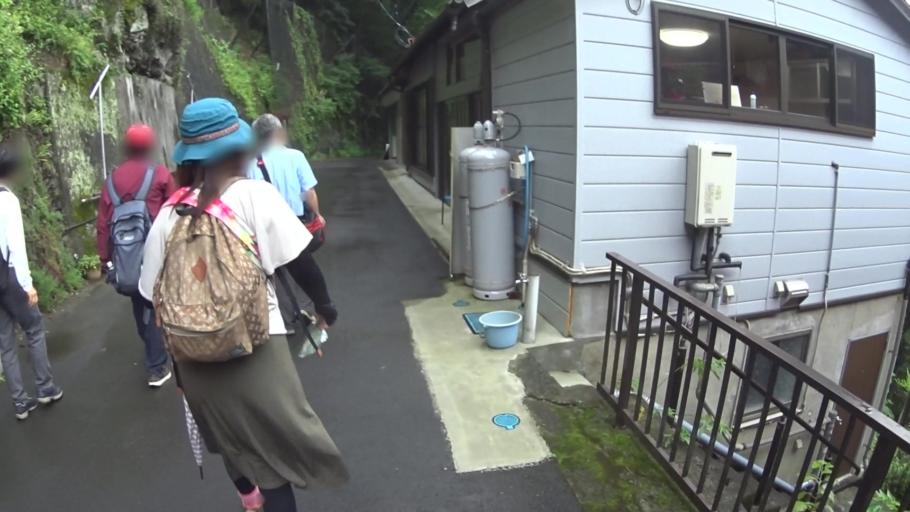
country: JP
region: Tokyo
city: Itsukaichi
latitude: 35.8004
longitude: 139.0776
